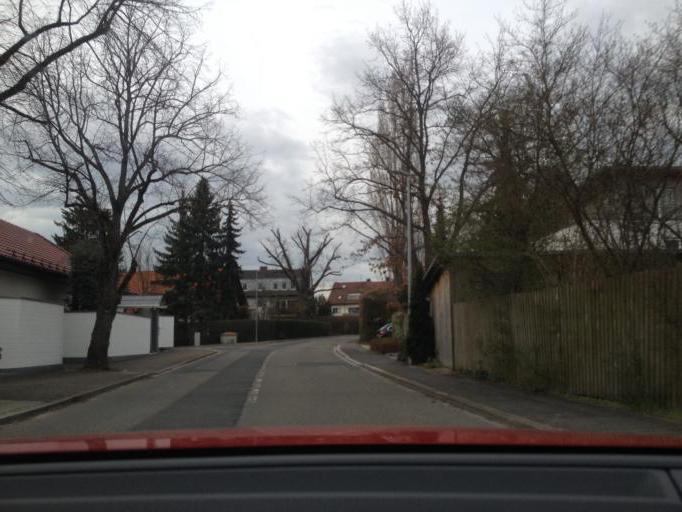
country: DE
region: Bavaria
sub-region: Regierungsbezirk Mittelfranken
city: Lauf an der Pegnitz
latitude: 49.5131
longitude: 11.2727
